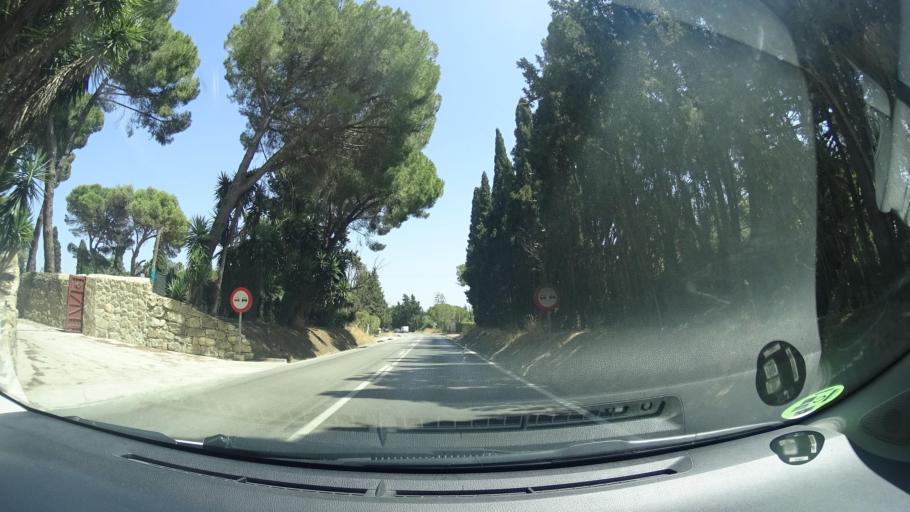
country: ES
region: Andalusia
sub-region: Provincia de Cadiz
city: Jerez de la Frontera
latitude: 36.6623
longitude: -6.1083
